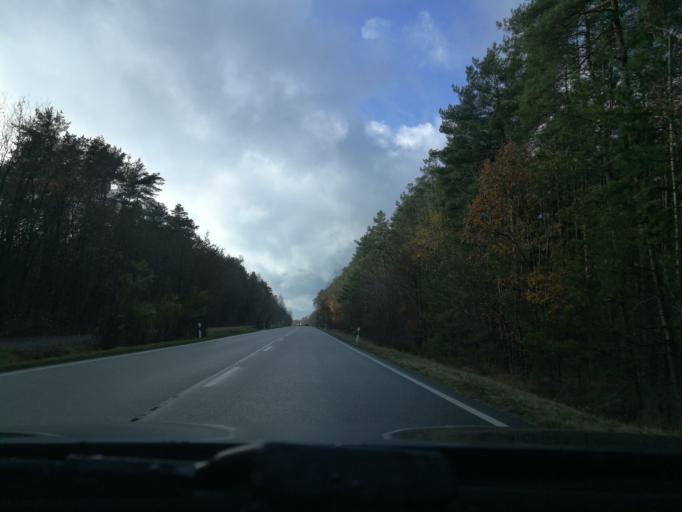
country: DE
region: Bavaria
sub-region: Regierungsbezirk Mittelfranken
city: Kammerstein
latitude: 49.2866
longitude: 10.9473
